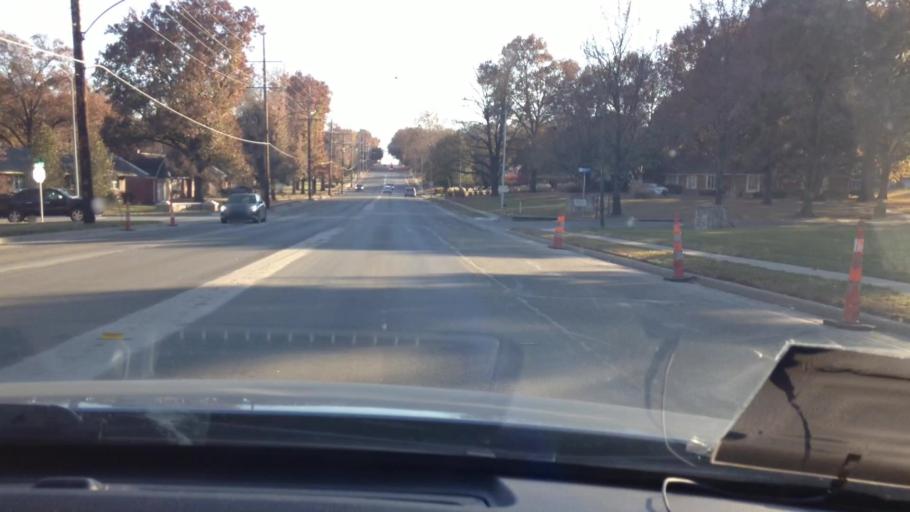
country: US
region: Kansas
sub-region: Johnson County
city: Leawood
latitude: 38.9682
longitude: -94.6304
